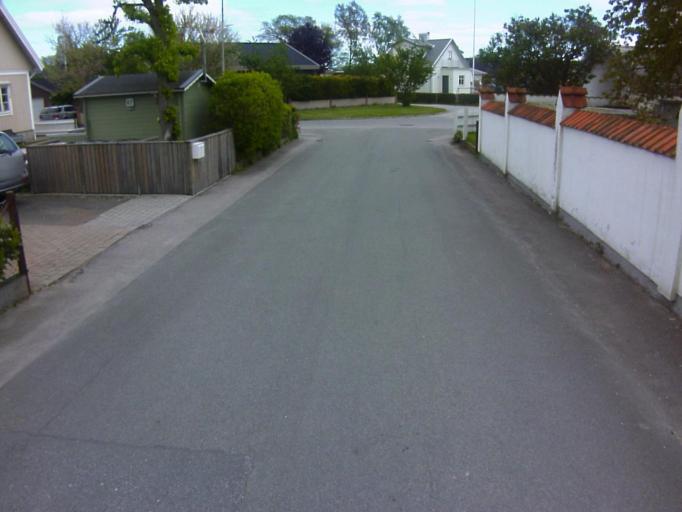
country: SE
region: Blekinge
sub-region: Solvesborgs Kommun
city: Soelvesborg
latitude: 56.0554
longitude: 14.5785
